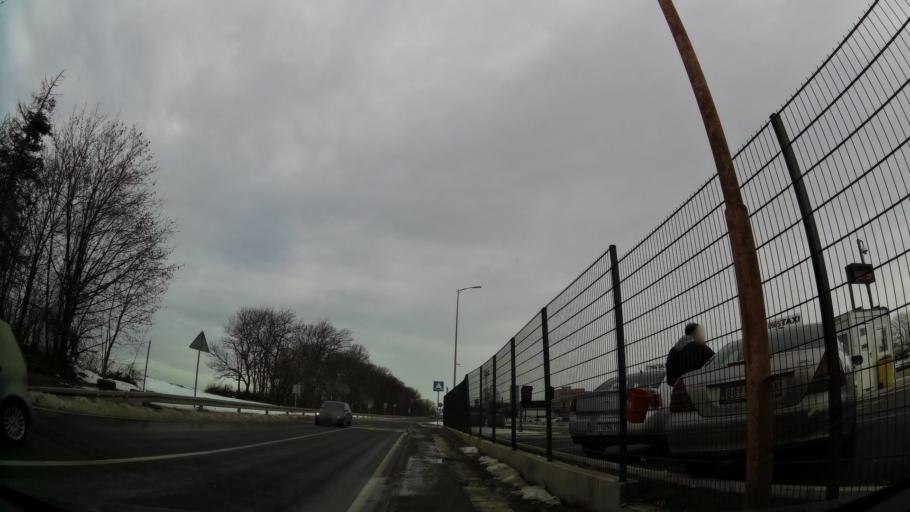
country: RS
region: Central Serbia
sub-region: Belgrade
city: Surcin
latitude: 44.8139
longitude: 20.2910
